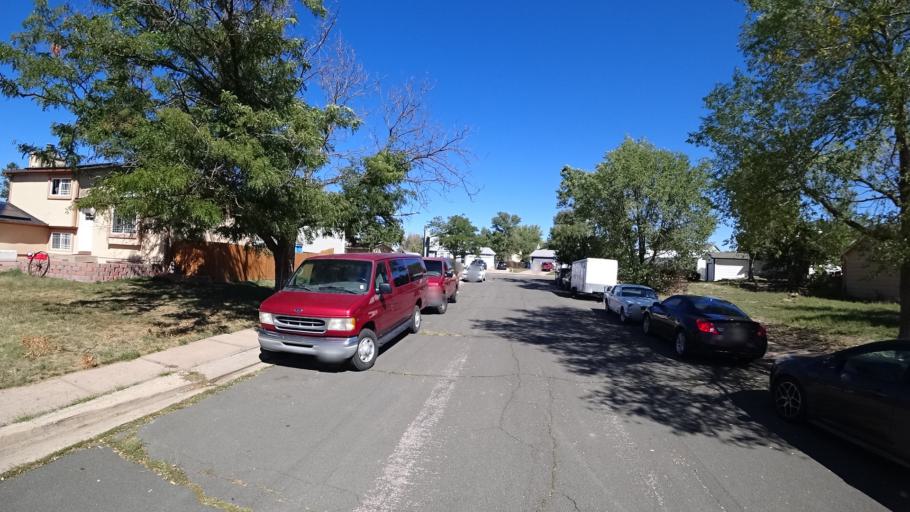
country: US
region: Colorado
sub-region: El Paso County
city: Cimarron Hills
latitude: 38.8161
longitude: -104.7378
